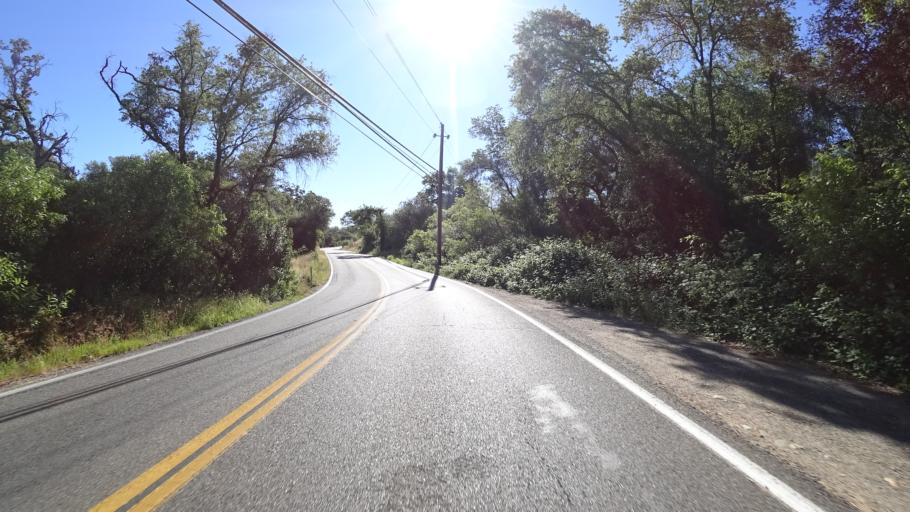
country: US
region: California
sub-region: Placer County
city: Newcastle
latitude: 38.8763
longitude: -121.1636
